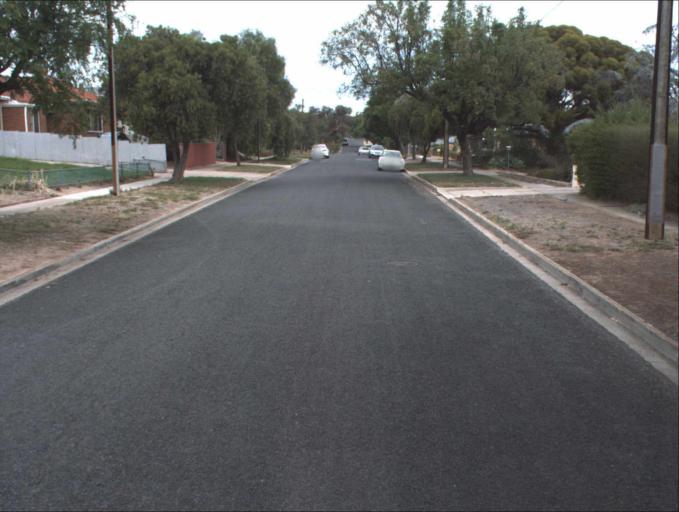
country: AU
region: South Australia
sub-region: Port Adelaide Enfield
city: Enfield
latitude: -34.8551
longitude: 138.6061
